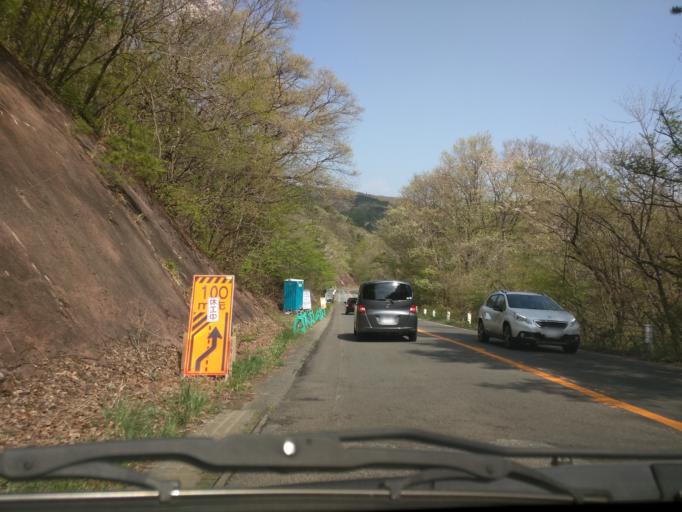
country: JP
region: Fukushima
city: Nihommatsu
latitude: 37.6010
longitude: 140.3724
